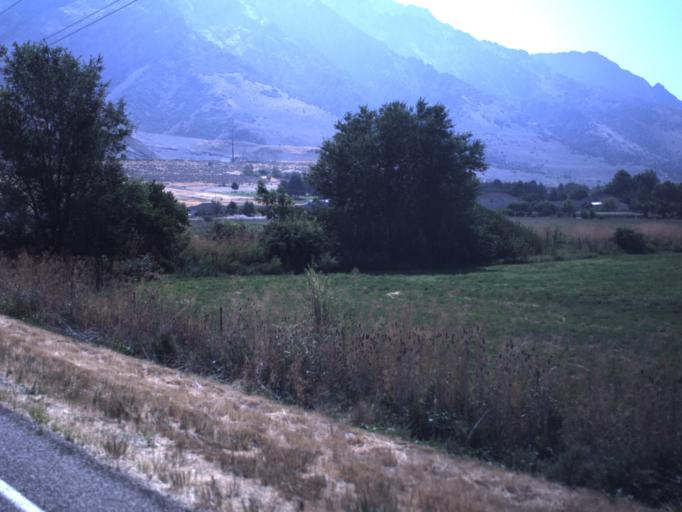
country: US
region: Utah
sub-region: Box Elder County
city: Willard
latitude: 41.4225
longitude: -112.0391
